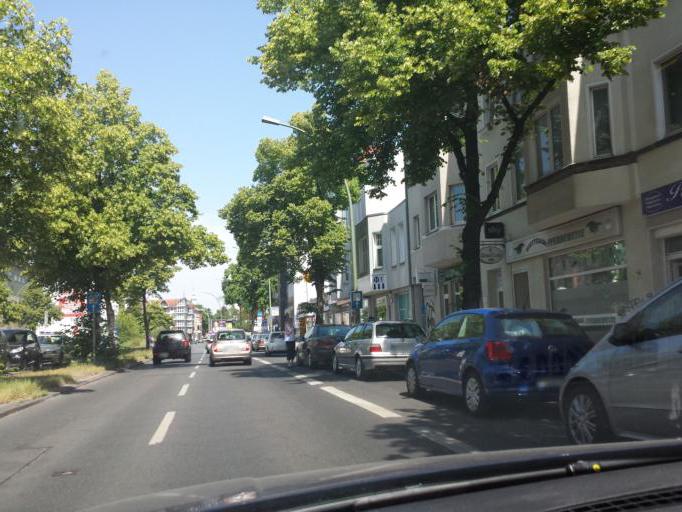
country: DE
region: Berlin
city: Mariendorf
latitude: 52.4360
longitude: 13.3892
